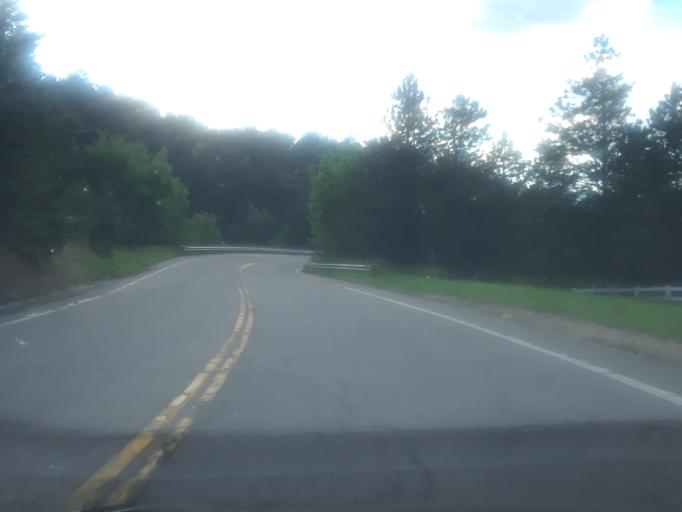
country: US
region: Colorado
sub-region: Jefferson County
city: Kittredge
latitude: 39.7077
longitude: -105.3437
